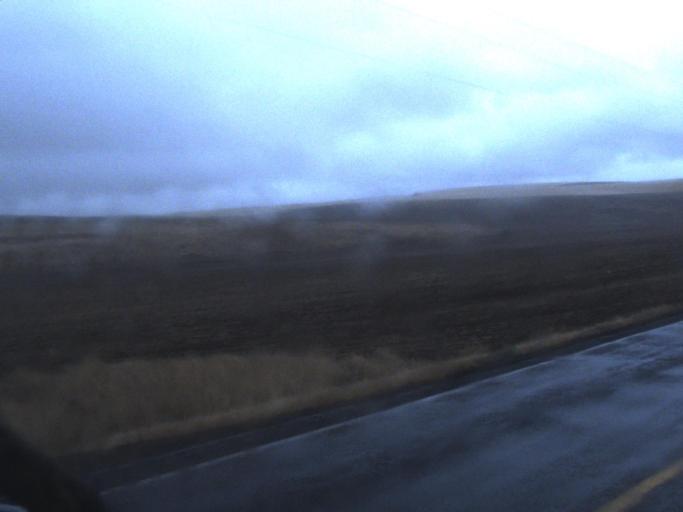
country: US
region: Washington
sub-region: Whitman County
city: Colfax
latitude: 47.0997
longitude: -117.6070
